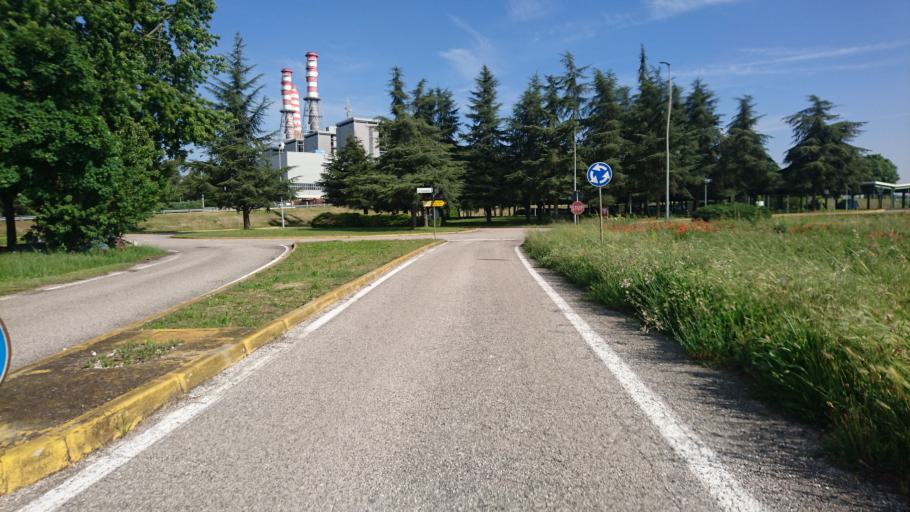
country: IT
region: Lombardy
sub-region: Provincia di Mantova
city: Carbonara di Po
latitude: 45.0228
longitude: 11.2552
